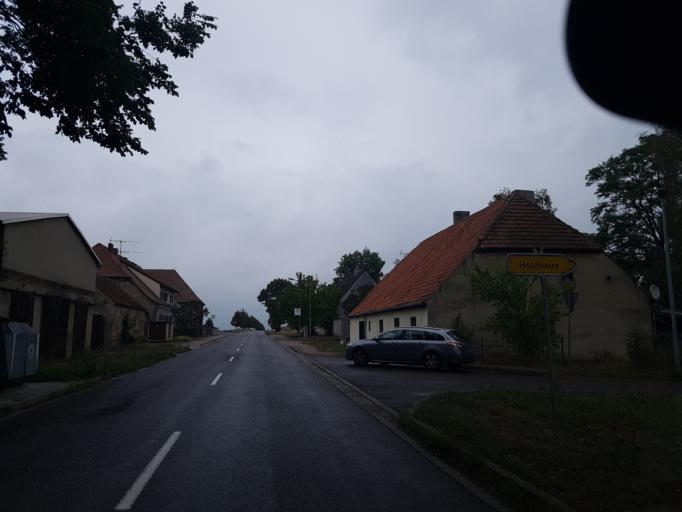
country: DE
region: Saxony-Anhalt
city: Tucheim
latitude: 52.2714
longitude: 12.1611
